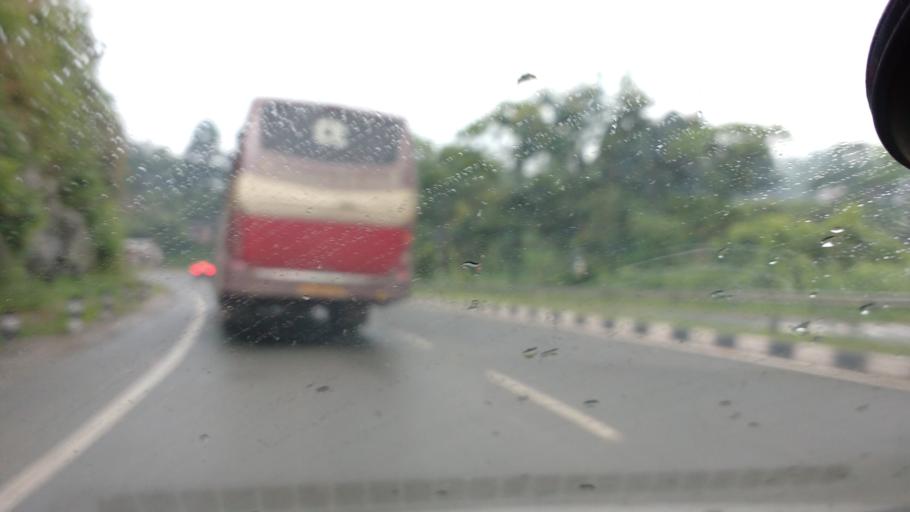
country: IN
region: Meghalaya
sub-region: Ri-Bhoi
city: Nongpoh
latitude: 25.8330
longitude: 91.8767
